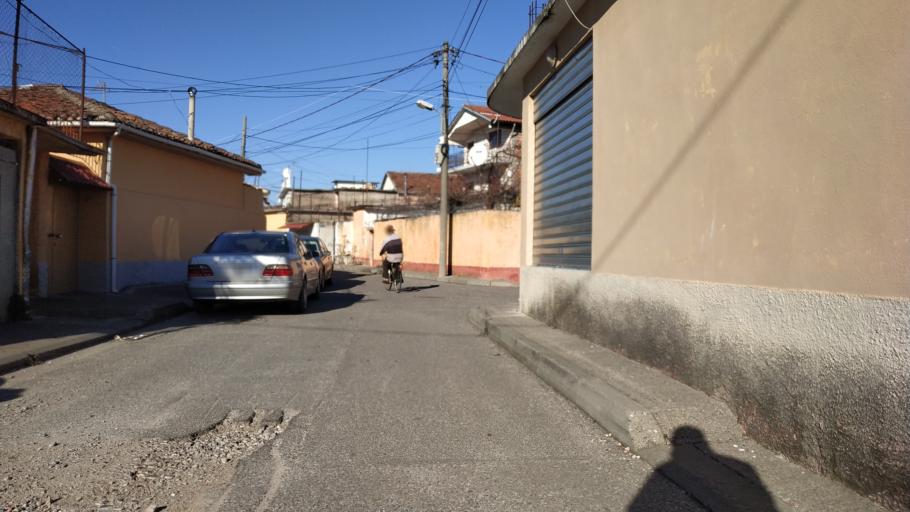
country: AL
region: Shkoder
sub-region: Rrethi i Shkodres
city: Shkoder
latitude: 42.0727
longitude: 19.5185
